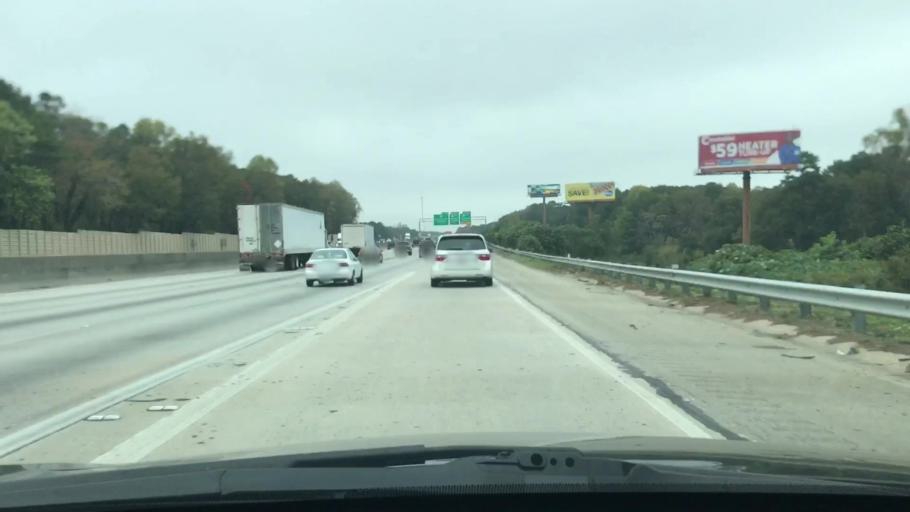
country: US
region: Georgia
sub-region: DeKalb County
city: Clarkston
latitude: 33.8076
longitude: -84.2504
